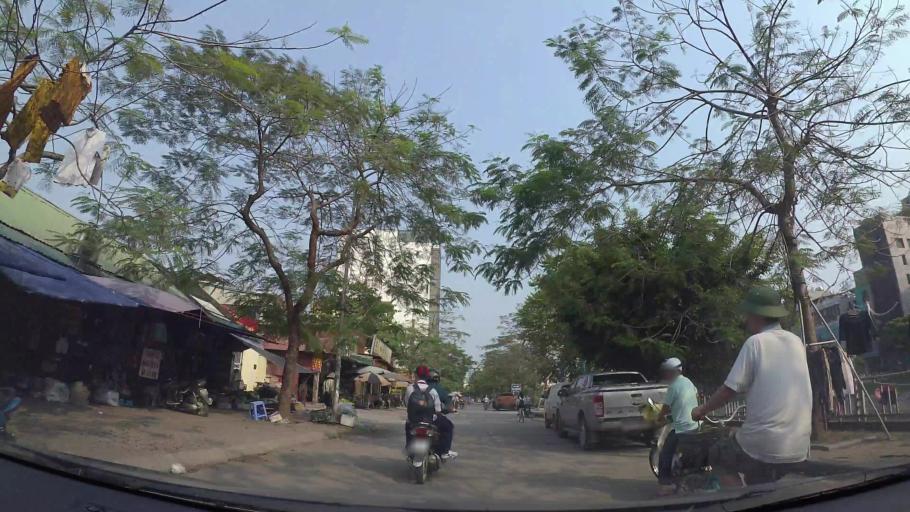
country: VN
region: Ha Noi
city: Thanh Xuan
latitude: 20.9814
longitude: 105.8180
